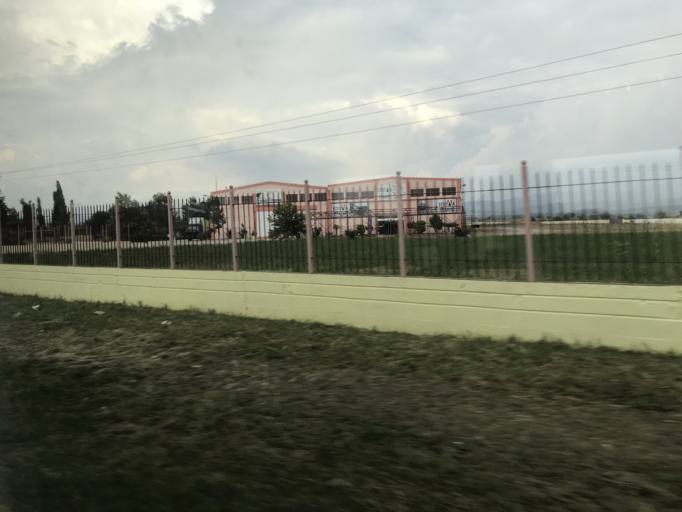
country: GR
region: East Macedonia and Thrace
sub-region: Nomos Rodopis
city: Sapes
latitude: 40.9742
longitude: 25.6446
